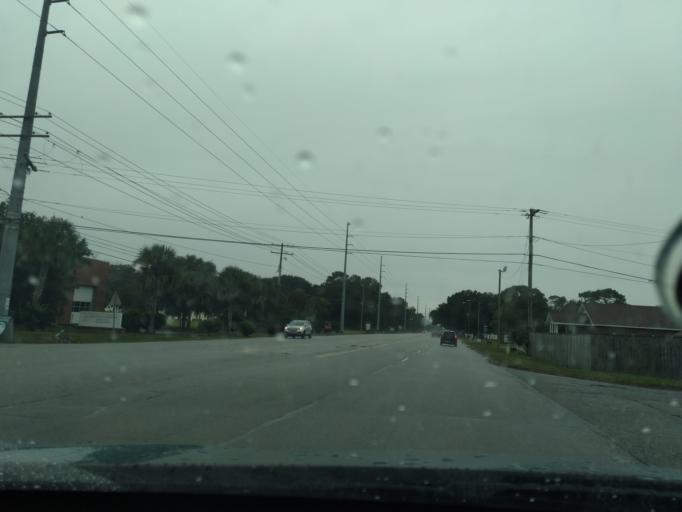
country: US
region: South Carolina
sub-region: Charleston County
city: Folly Beach
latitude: 32.7096
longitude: -79.9639
